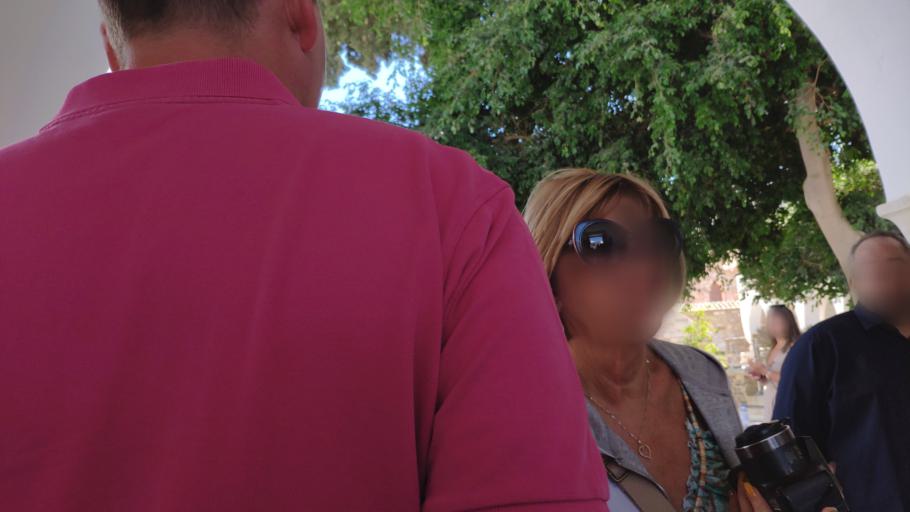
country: GR
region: South Aegean
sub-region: Nomos Kykladon
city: Paros
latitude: 37.0850
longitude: 25.1514
